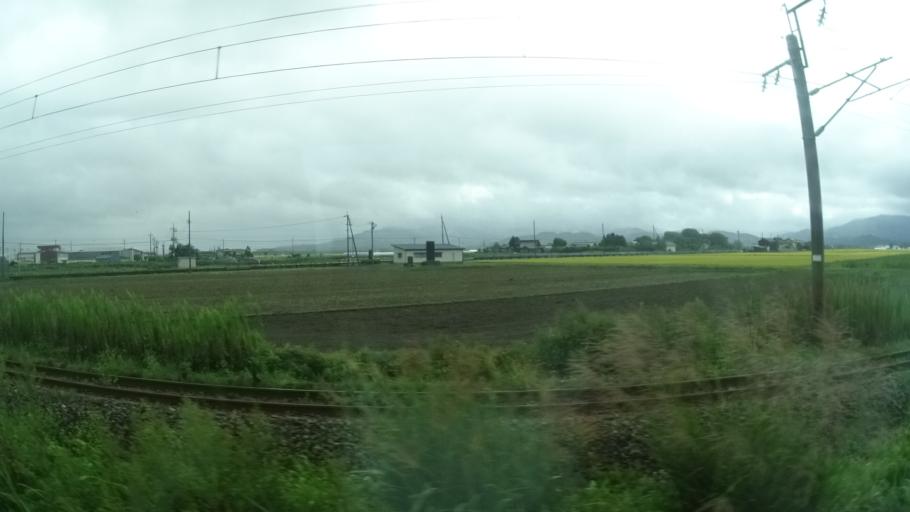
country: JP
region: Yamagata
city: Tsuruoka
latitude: 38.7413
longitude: 139.7593
